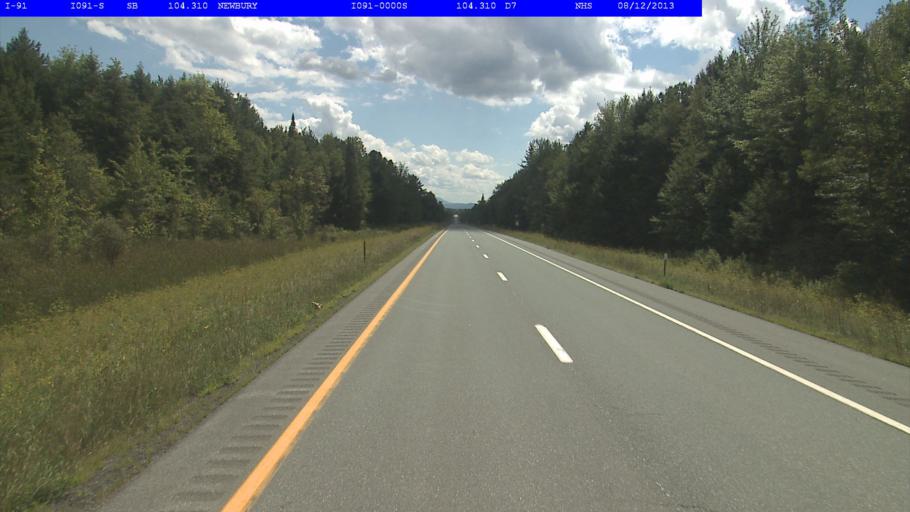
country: US
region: New Hampshire
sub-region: Grafton County
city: Haverhill
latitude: 44.0758
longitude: -72.1129
